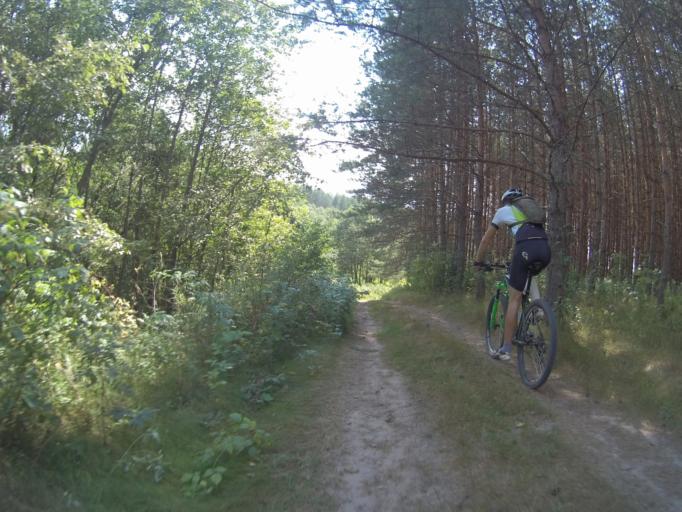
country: RU
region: Vladimir
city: Kideksha
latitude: 56.4163
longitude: 40.5528
